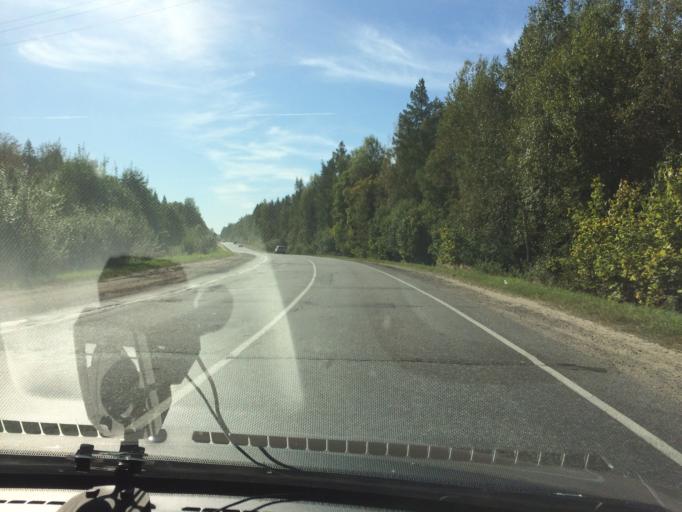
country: RU
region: Mariy-El
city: Yoshkar-Ola
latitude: 56.5712
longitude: 47.9708
